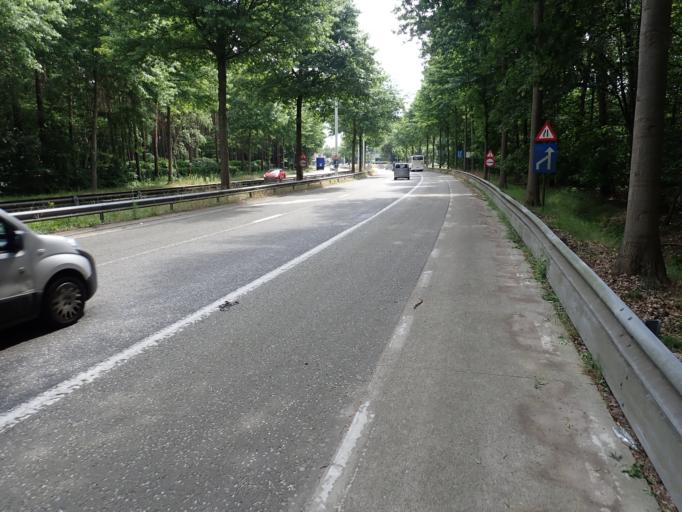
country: BE
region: Flanders
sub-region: Provincie Antwerpen
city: Wijnegem
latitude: 51.2315
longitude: 4.5473
